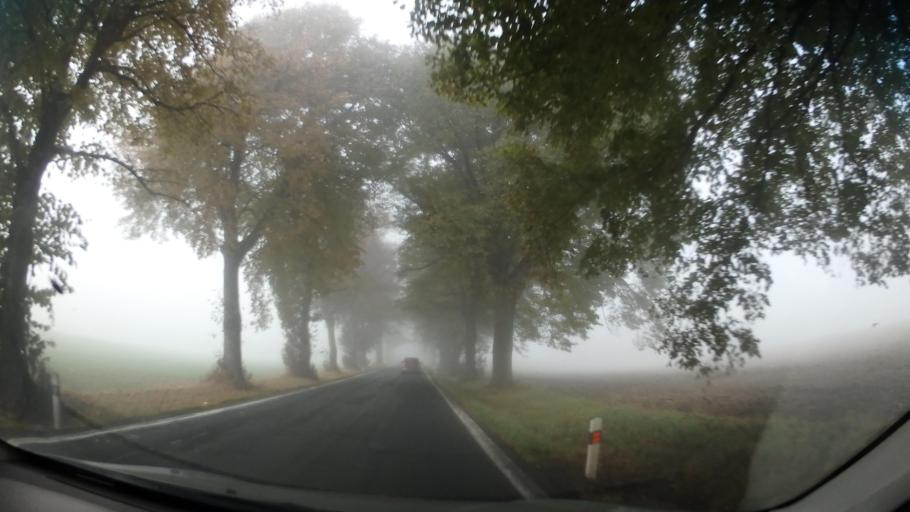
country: CZ
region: Vysocina
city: Krizanov
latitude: 49.4692
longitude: 16.0966
